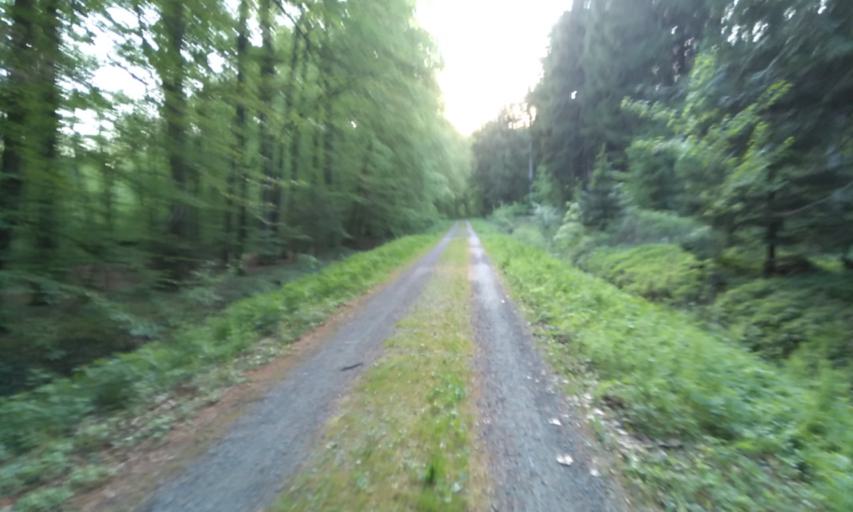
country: DE
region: Lower Saxony
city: Harsefeld
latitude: 53.4204
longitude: 9.4928
